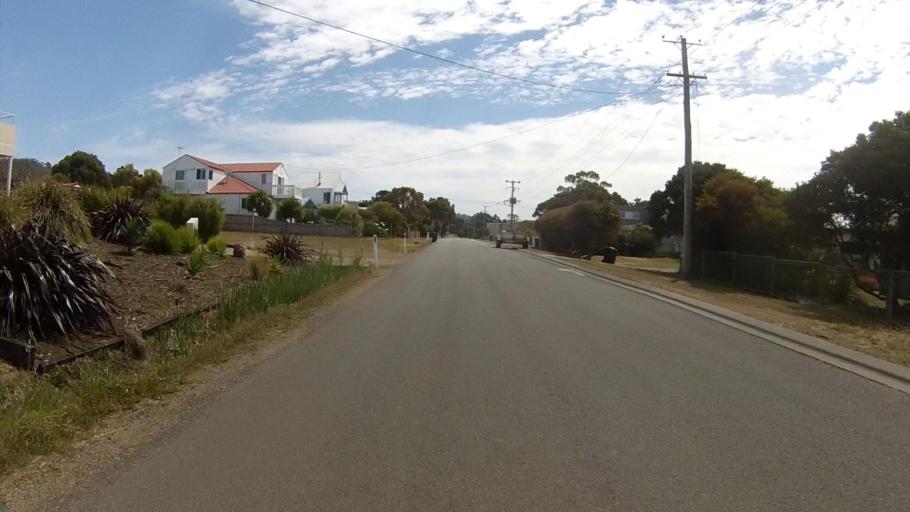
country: AU
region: Tasmania
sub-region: Clarence
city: Sandford
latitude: -42.9902
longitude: 147.5224
